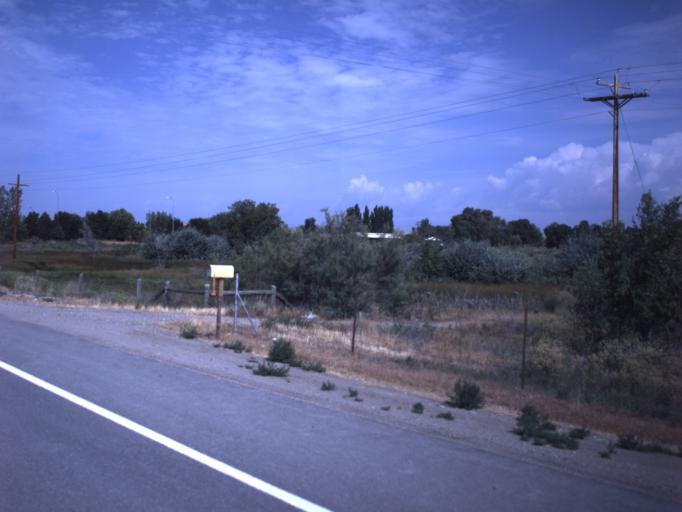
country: US
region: Utah
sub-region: Uintah County
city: Naples
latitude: 40.3699
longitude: -109.3406
